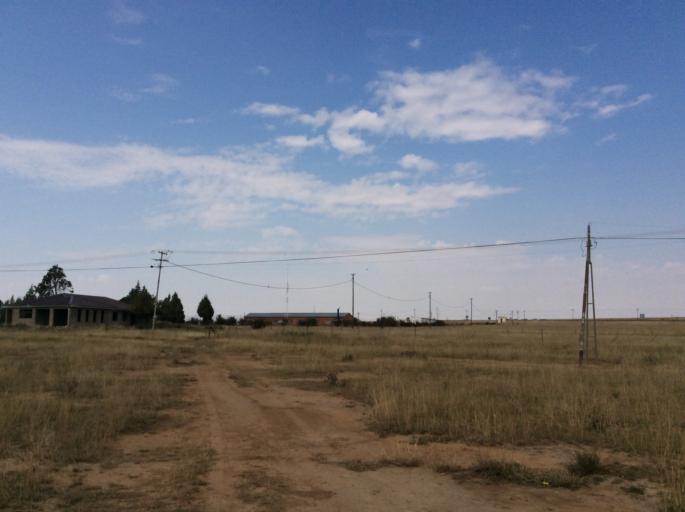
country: LS
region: Mafeteng
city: Mafeteng
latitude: -29.7337
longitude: 27.0273
